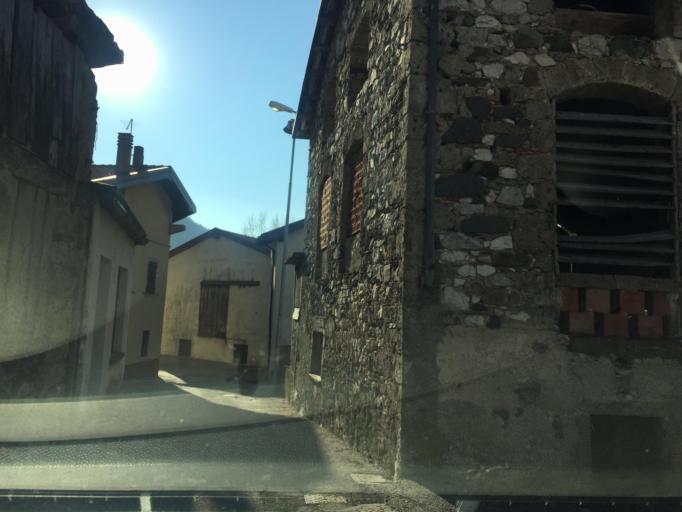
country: IT
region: Friuli Venezia Giulia
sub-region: Provincia di Udine
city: Zuglio
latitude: 46.4300
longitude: 13.0561
